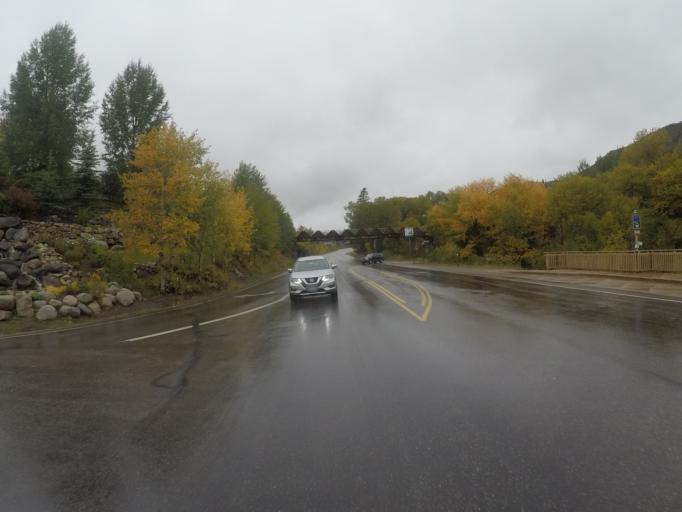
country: US
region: Colorado
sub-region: Pitkin County
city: Snowmass Village
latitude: 39.2111
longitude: -106.9426
